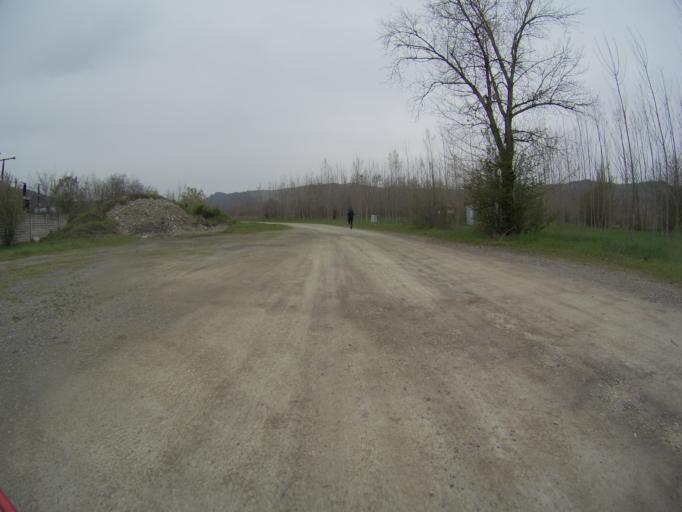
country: IT
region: Emilia-Romagna
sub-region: Provincia di Reggio Emilia
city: Ciano d'Enza
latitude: 44.5959
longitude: 10.4056
